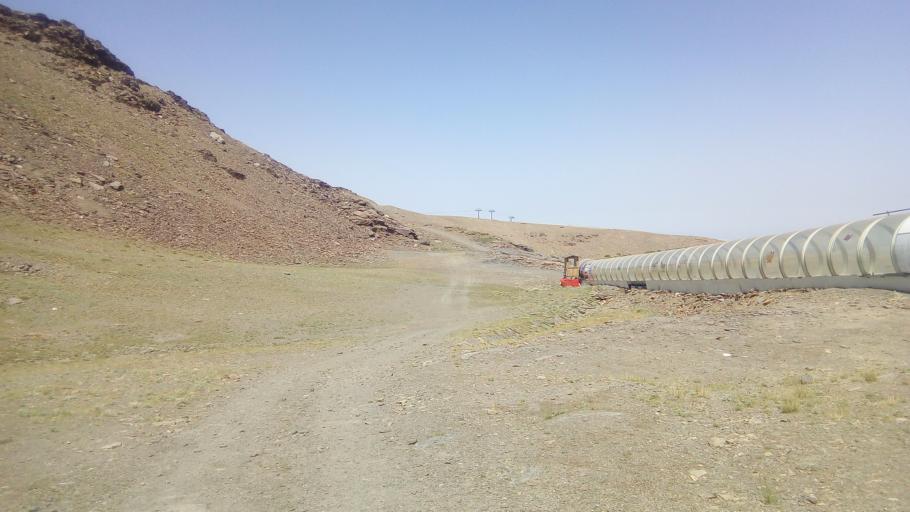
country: ES
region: Andalusia
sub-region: Provincia de Granada
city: Guejar-Sierra
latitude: 37.0710
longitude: -3.3912
